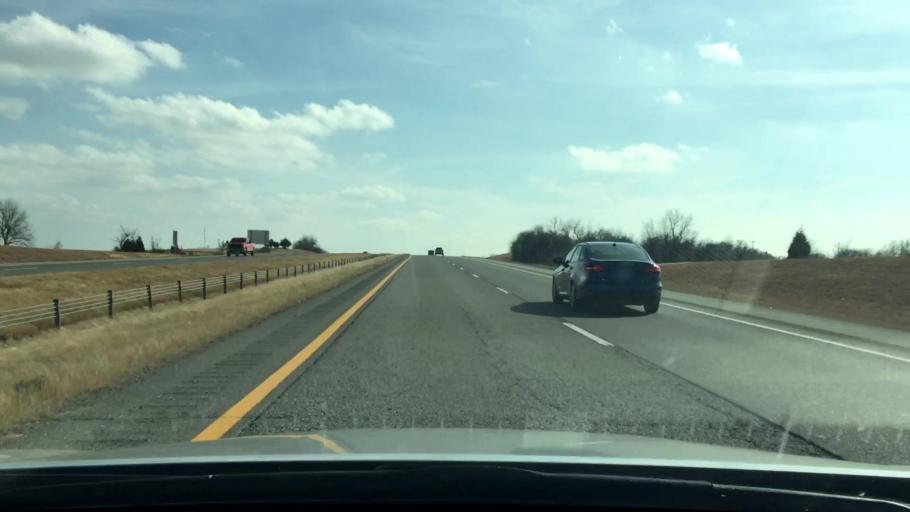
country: US
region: Oklahoma
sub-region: McClain County
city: Purcell
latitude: 34.9651
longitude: -97.3700
